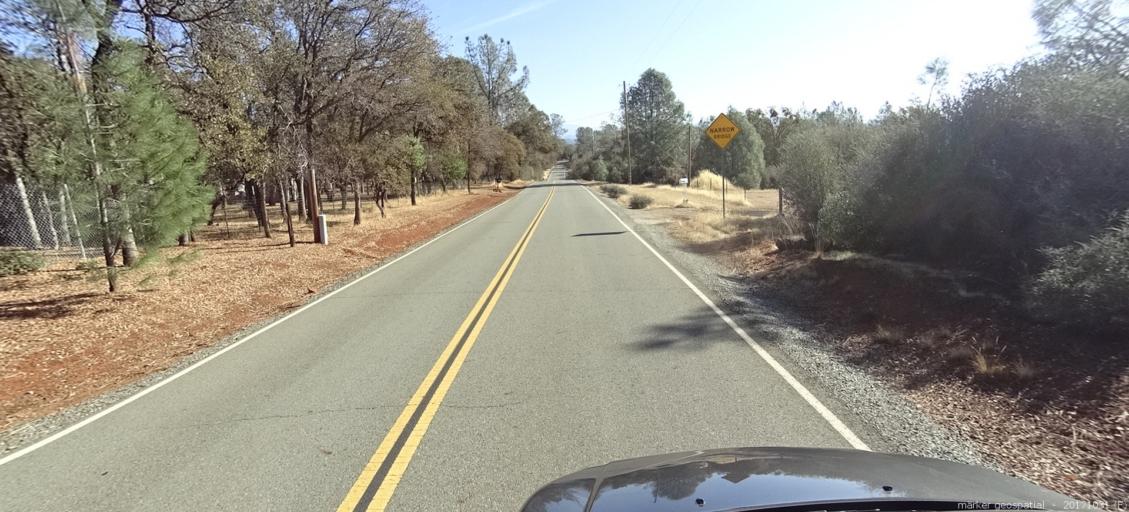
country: US
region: California
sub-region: Shasta County
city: Shingletown
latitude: 40.4463
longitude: -121.8950
